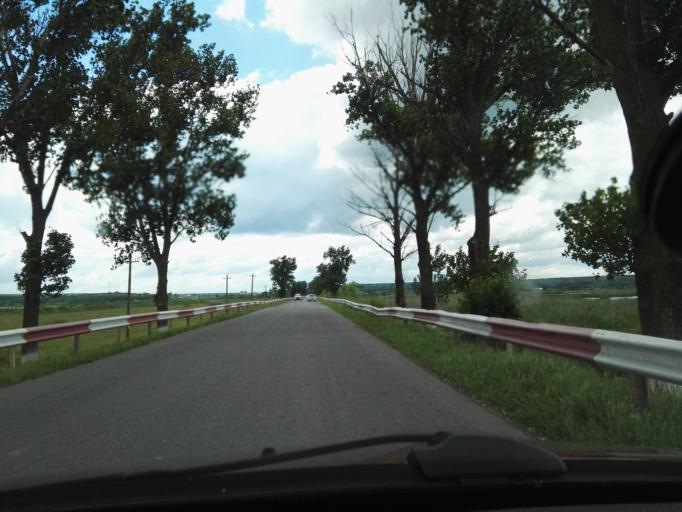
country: RO
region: Giurgiu
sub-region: Comuna Comana
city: Comana
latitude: 44.1889
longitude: 26.1339
